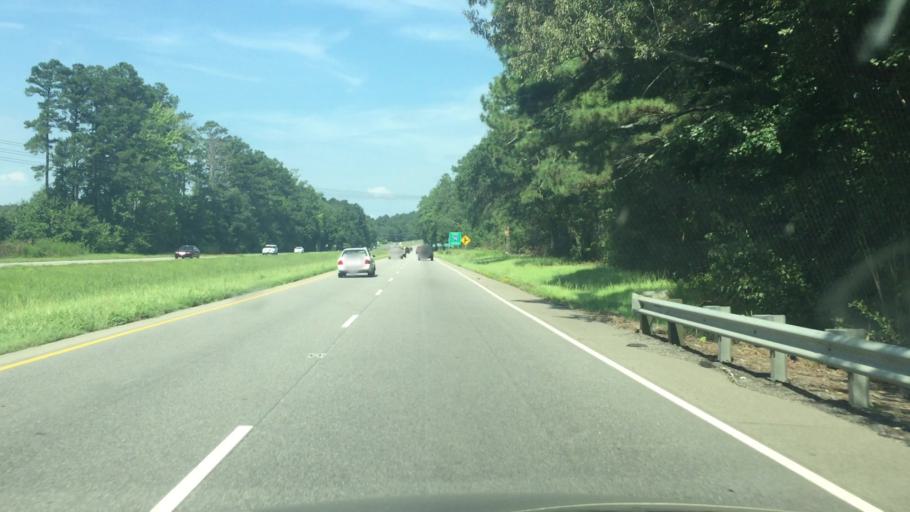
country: US
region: North Carolina
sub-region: Scotland County
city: Laurel Hill
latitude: 34.7993
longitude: -79.5244
